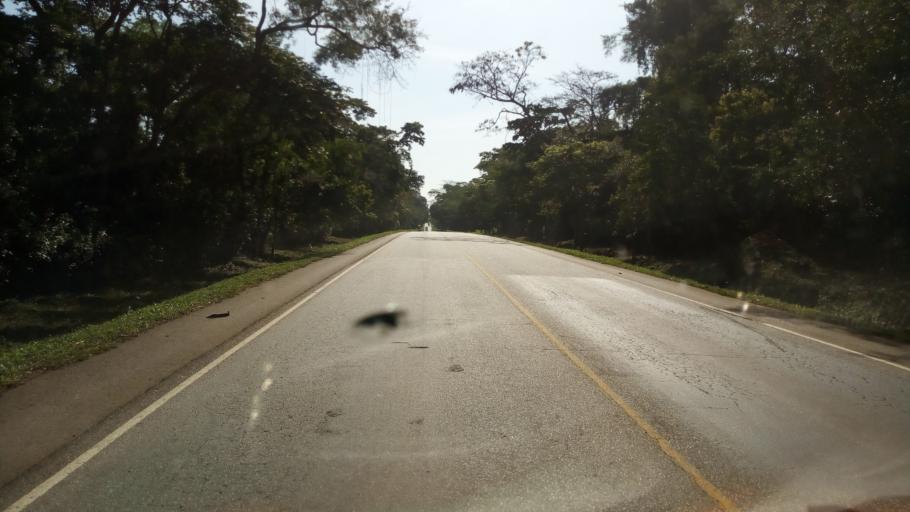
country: UG
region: Eastern Region
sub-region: Busia District
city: Busia
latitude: 0.5370
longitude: 34.0020
